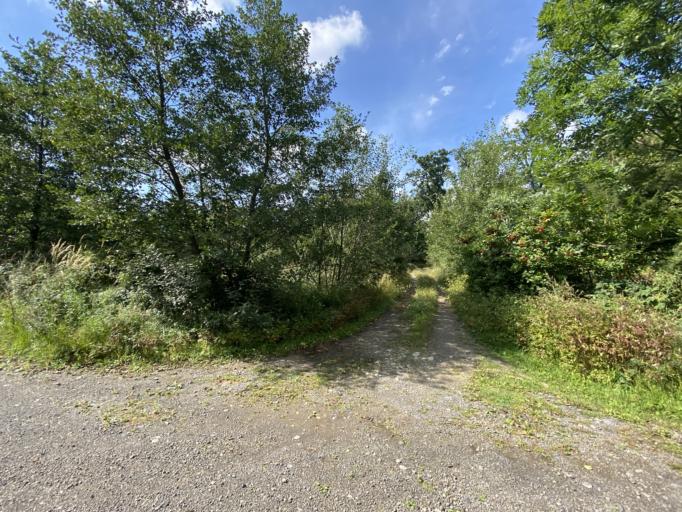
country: AT
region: Burgenland
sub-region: Politischer Bezirk Oberpullendorf
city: Kobersdorf
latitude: 47.5801
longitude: 16.3744
